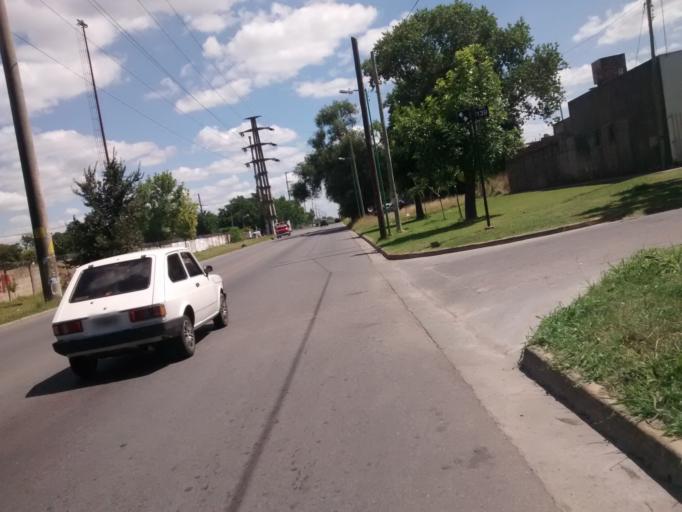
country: AR
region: Buenos Aires
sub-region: Partido de La Plata
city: La Plata
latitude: -34.9461
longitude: -57.9818
